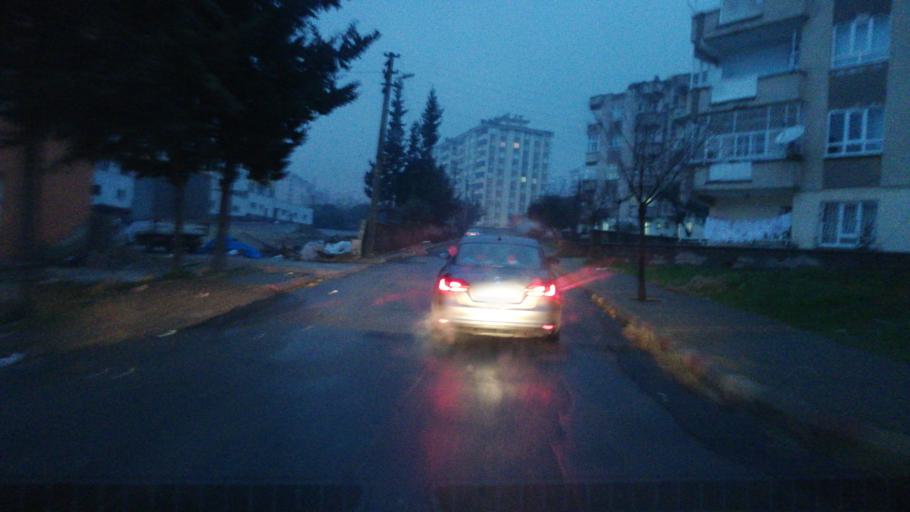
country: TR
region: Kahramanmaras
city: Kahramanmaras
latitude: 37.5947
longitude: 36.8951
